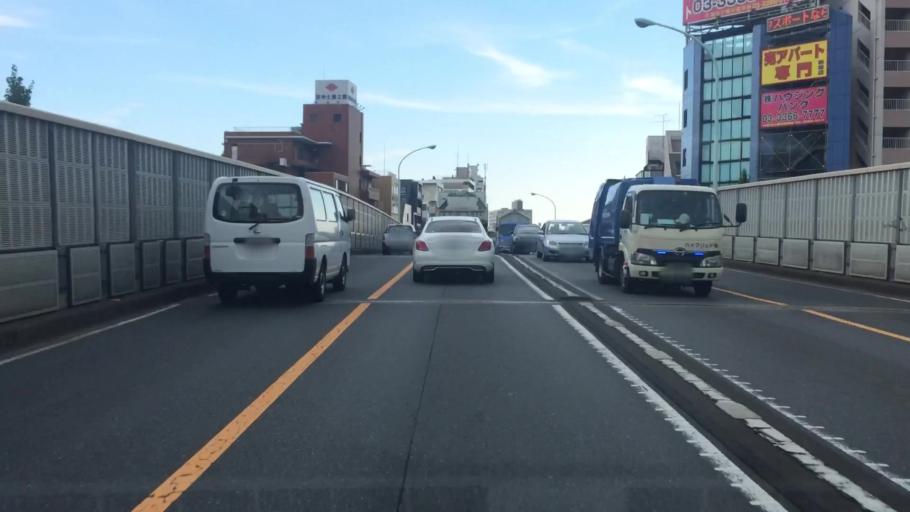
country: JP
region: Tokyo
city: Tokyo
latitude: 35.6984
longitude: 139.6547
